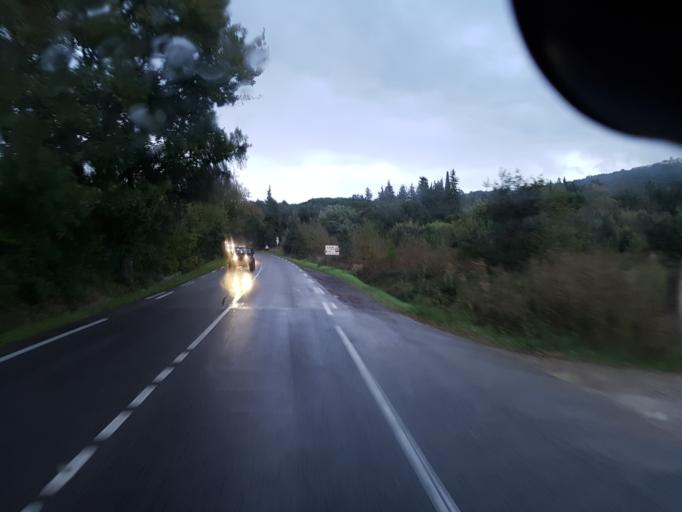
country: FR
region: Provence-Alpes-Cote d'Azur
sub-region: Departement du Var
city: Gassin
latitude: 43.2238
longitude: 6.5704
